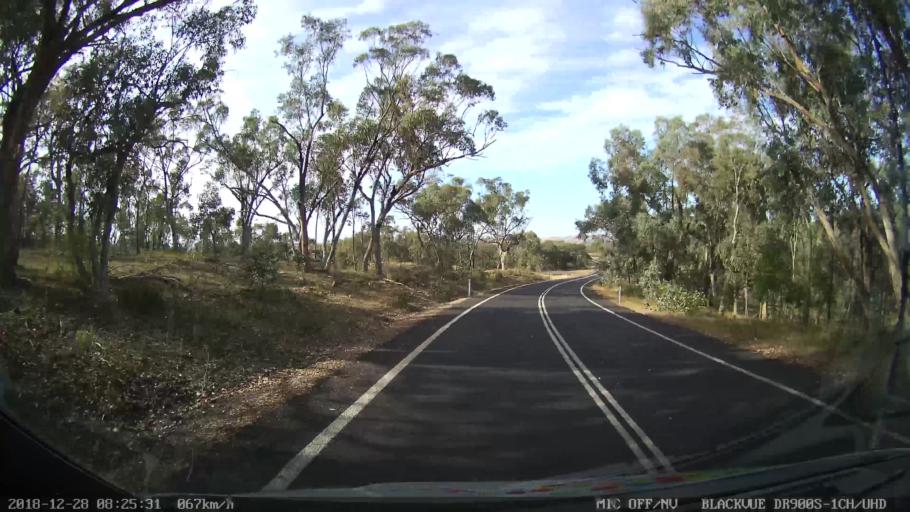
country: AU
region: New South Wales
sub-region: Blayney
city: Blayney
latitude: -33.9270
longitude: 149.3522
